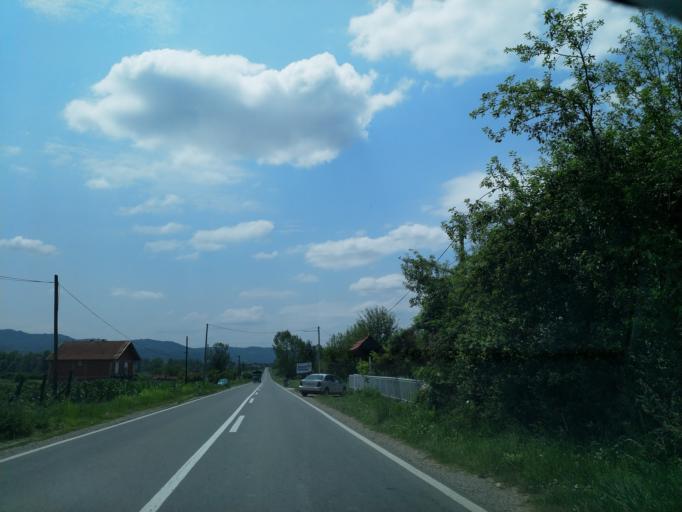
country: RS
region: Central Serbia
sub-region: Rasinski Okrug
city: Krusevac
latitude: 43.4621
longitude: 21.2476
